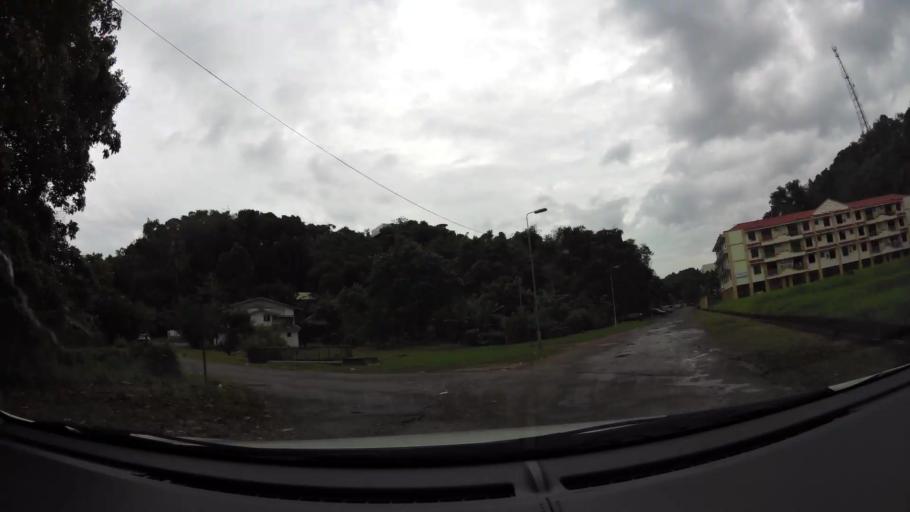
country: BN
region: Brunei and Muara
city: Bandar Seri Begawan
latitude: 4.8961
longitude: 114.9423
